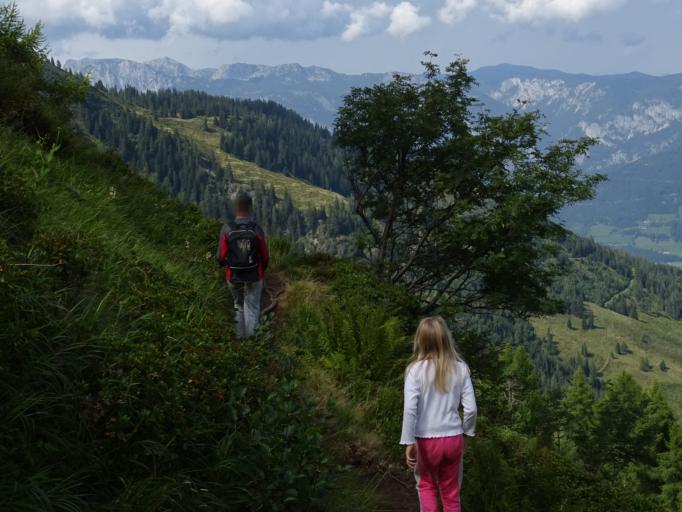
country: AT
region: Styria
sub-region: Politischer Bezirk Liezen
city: Haus
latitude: 47.3635
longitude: 13.7901
